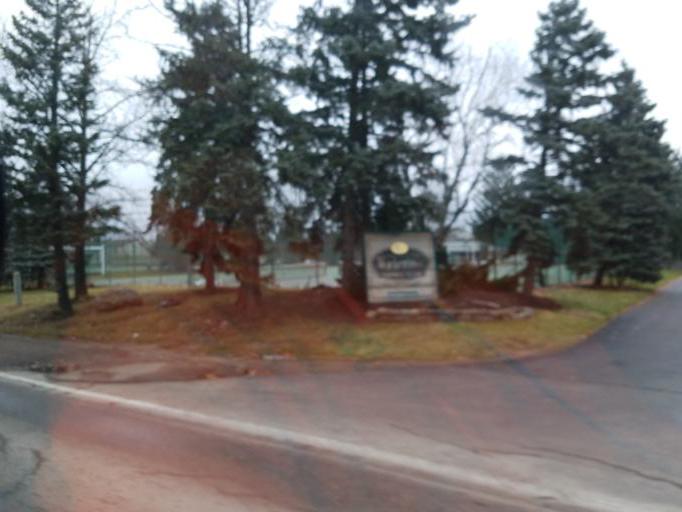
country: US
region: Ohio
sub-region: Franklin County
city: Minerva Park
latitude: 40.0882
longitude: -82.9602
